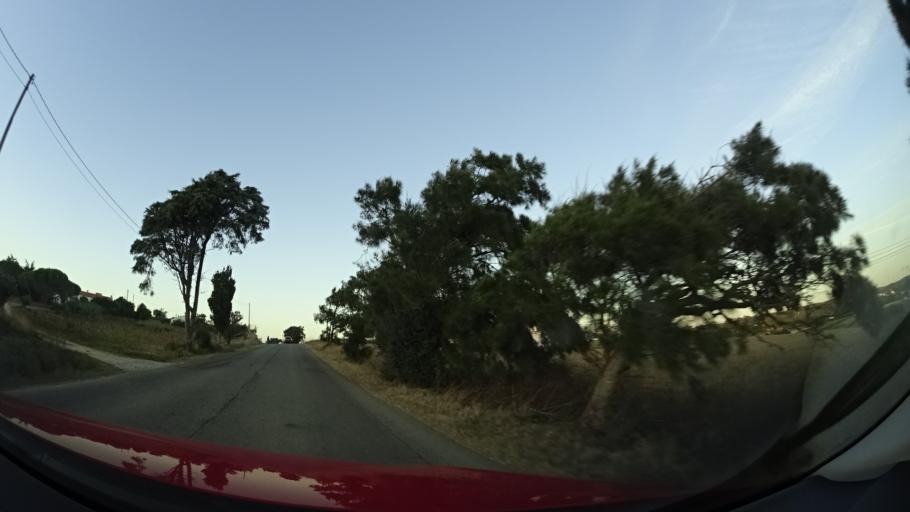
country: PT
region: Faro
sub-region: Aljezur
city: Aljezur
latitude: 37.2301
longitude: -8.8300
